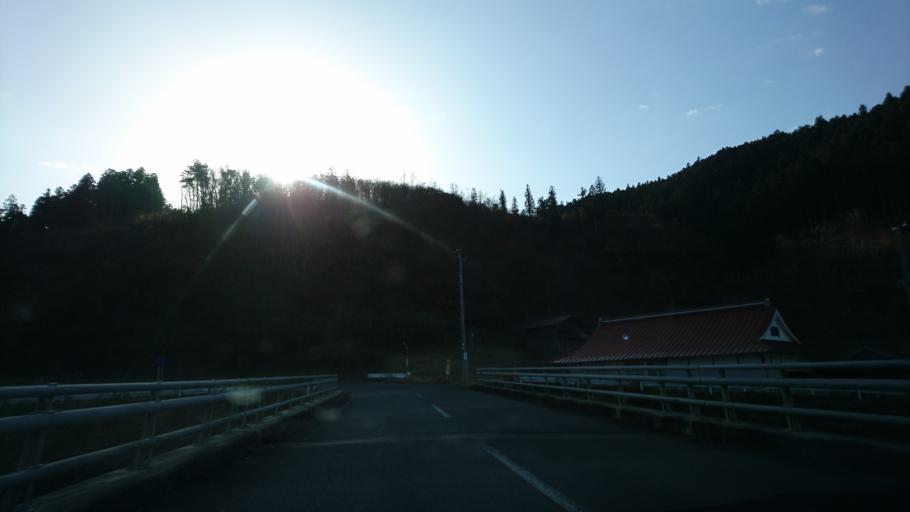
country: JP
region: Iwate
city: Ichinoseki
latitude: 38.8948
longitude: 141.2774
